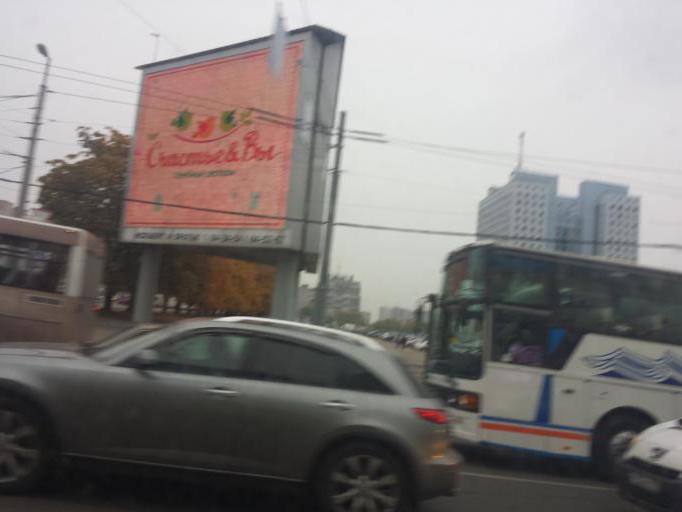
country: RU
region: Kaliningrad
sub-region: Gorod Kaliningrad
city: Kaliningrad
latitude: 54.7112
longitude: 20.5091
